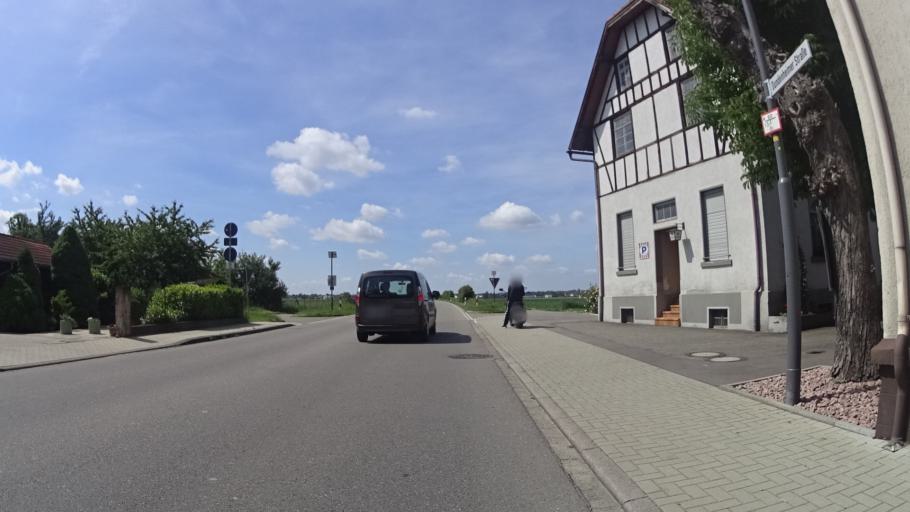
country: DE
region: Baden-Wuerttemberg
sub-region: Freiburg Region
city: Meissenheim
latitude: 48.4478
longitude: 7.8149
